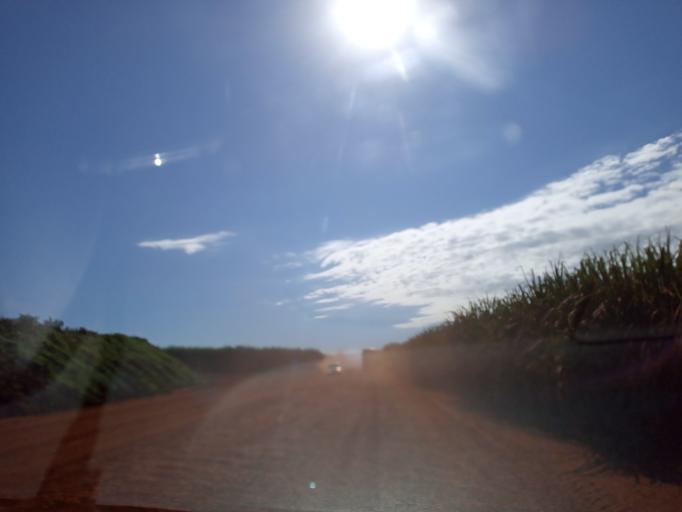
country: BR
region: Goias
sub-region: Itumbiara
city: Itumbiara
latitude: -18.4508
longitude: -49.1831
